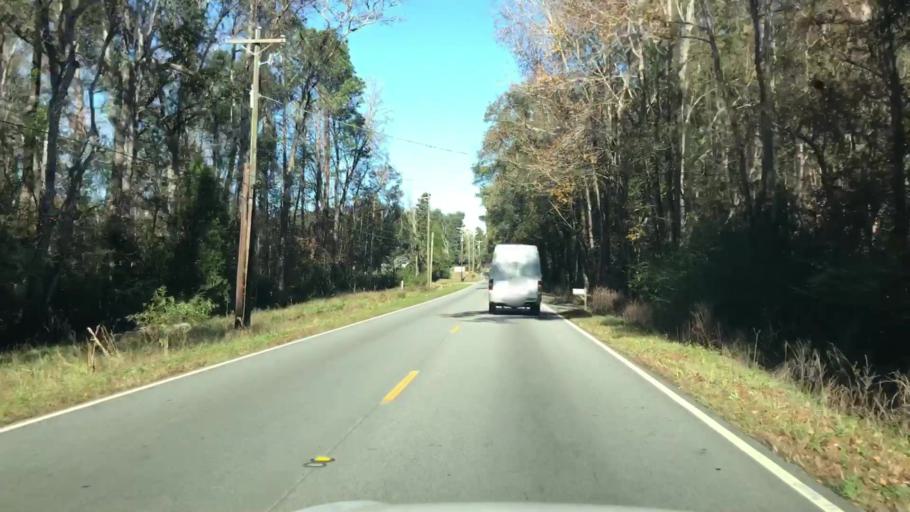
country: US
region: South Carolina
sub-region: Dorchester County
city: Centerville
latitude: 32.9778
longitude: -80.2147
